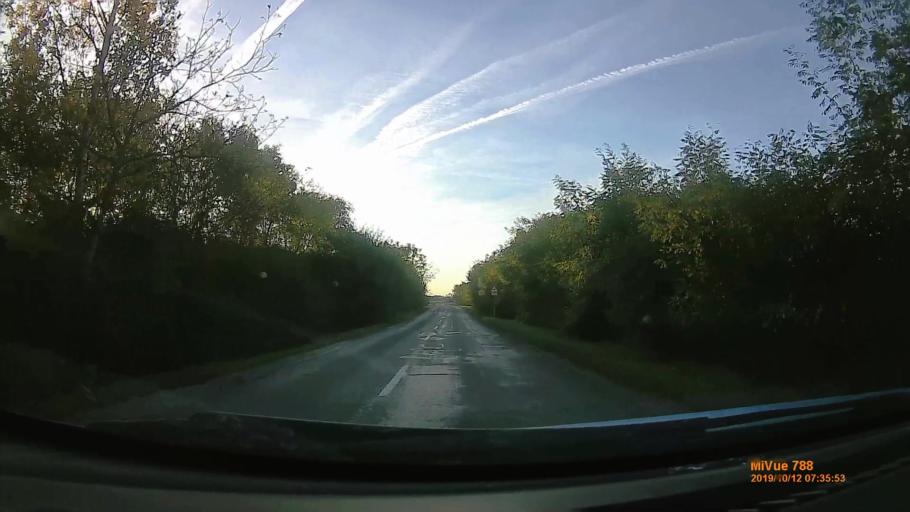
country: HU
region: Hajdu-Bihar
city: Pocsaj
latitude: 47.2501
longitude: 21.8112
